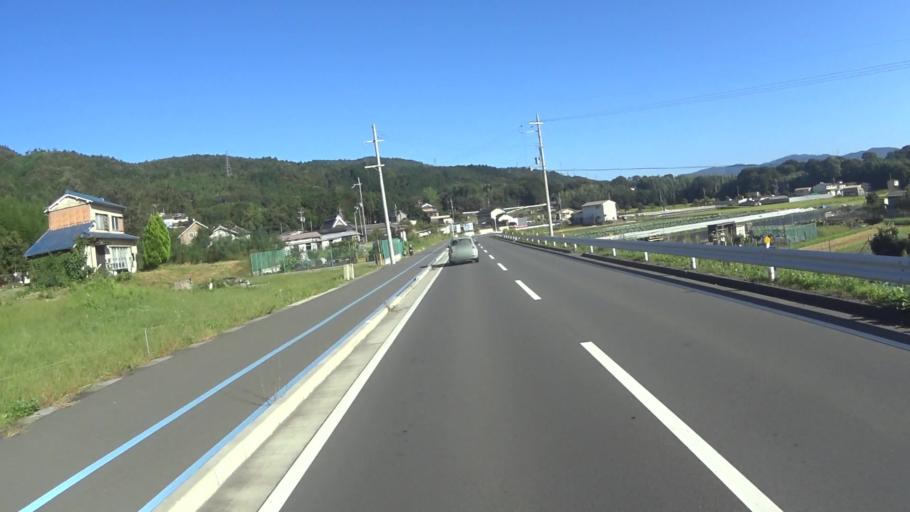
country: JP
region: Kyoto
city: Kameoka
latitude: 35.0314
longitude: 135.5849
